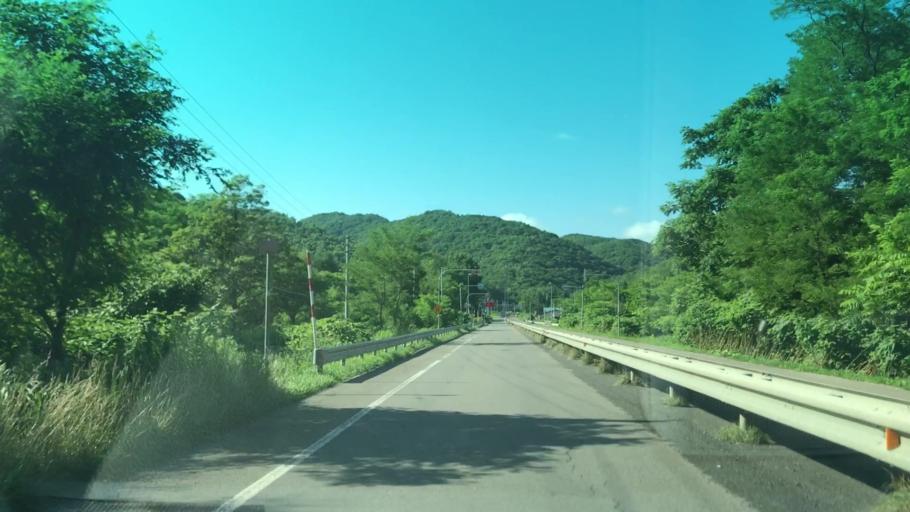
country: JP
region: Hokkaido
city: Iwanai
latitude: 43.0028
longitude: 140.6682
